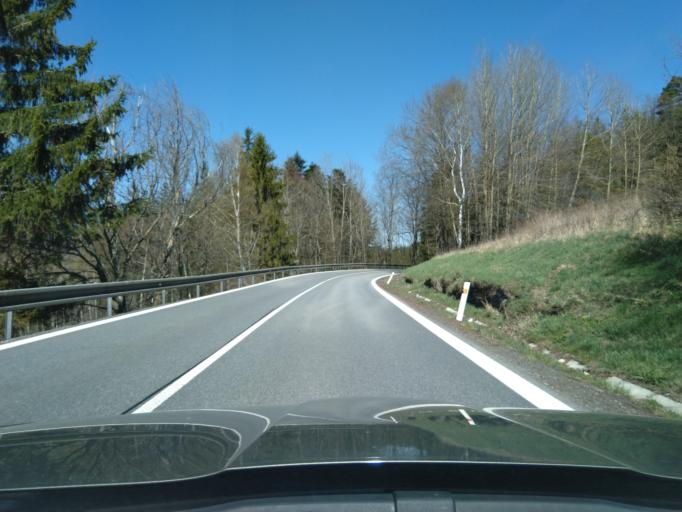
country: CZ
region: Jihocesky
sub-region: Okres Prachatice
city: Vimperk
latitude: 49.0353
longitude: 13.7619
